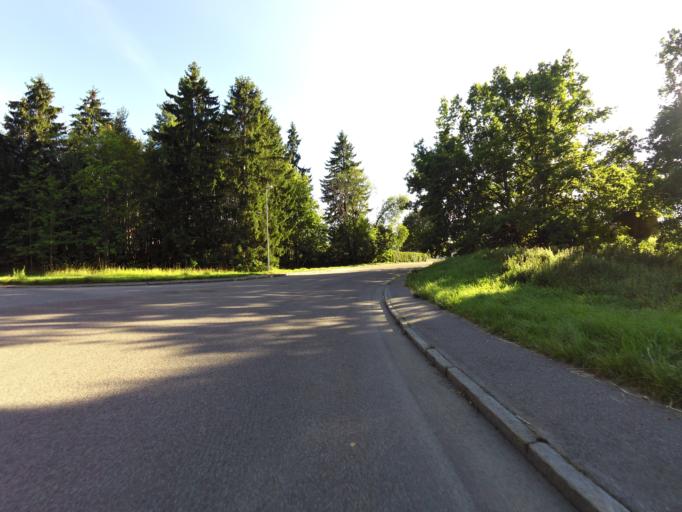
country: SE
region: Gaevleborg
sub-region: Gavle Kommun
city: Gavle
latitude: 60.6586
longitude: 17.1487
